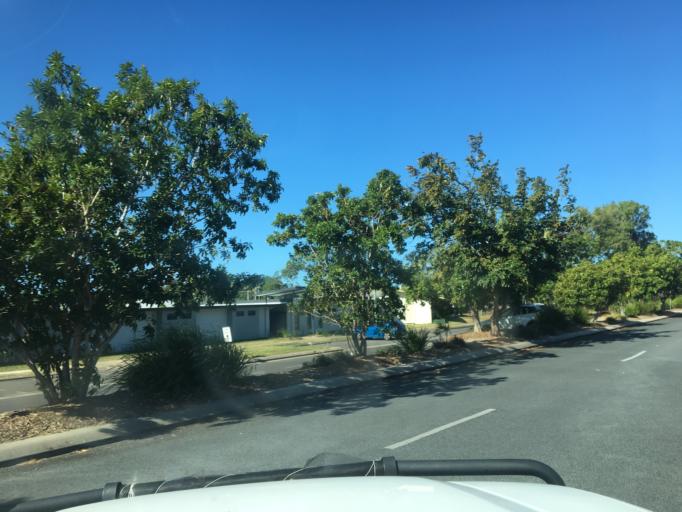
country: AU
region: Queensland
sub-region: Cairns
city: Cairns
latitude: -16.9118
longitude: 145.7466
